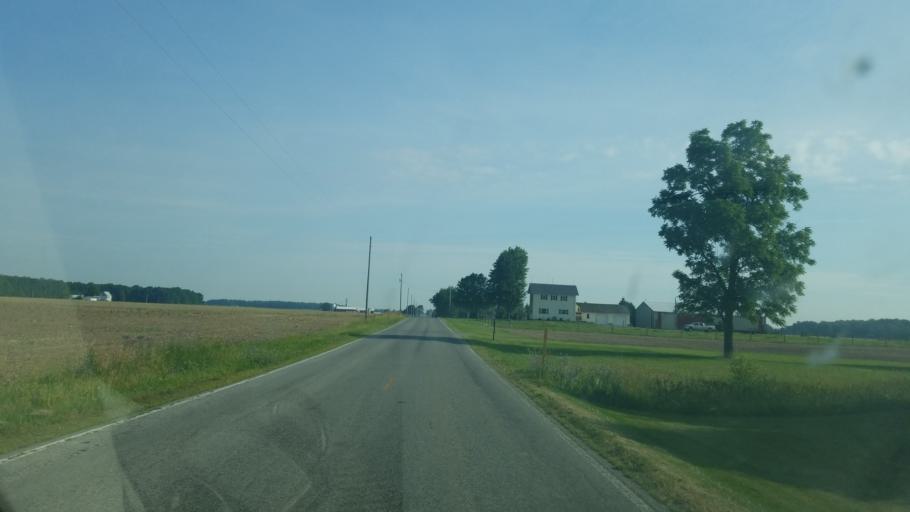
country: US
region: Ohio
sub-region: Hancock County
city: Arlington
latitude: 40.9149
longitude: -83.6987
